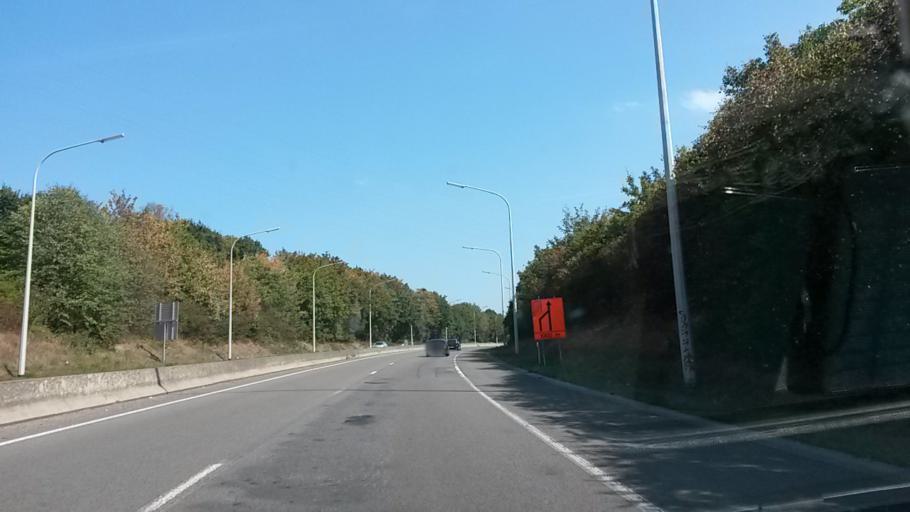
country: BE
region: Wallonia
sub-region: Province du Hainaut
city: Farciennes
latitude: 50.4258
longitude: 4.5201
